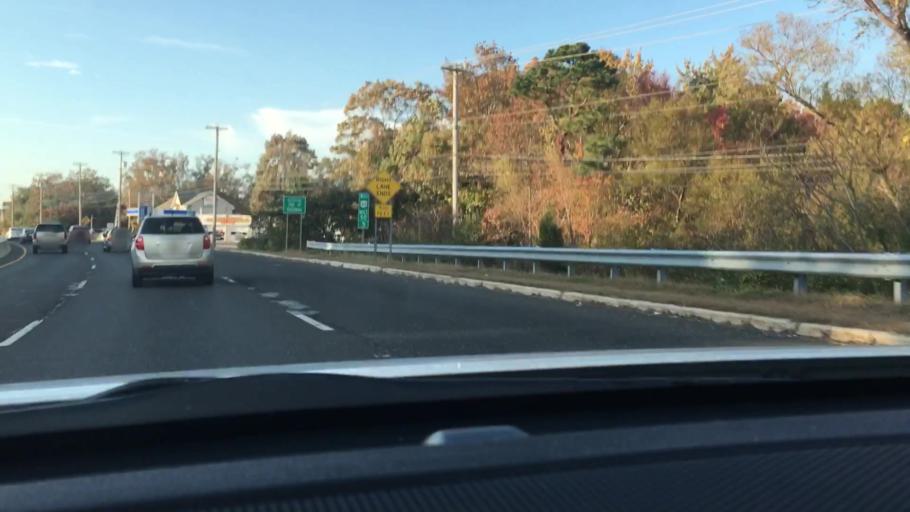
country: US
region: New Jersey
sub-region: Atlantic County
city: Absecon
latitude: 39.4390
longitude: -74.5183
